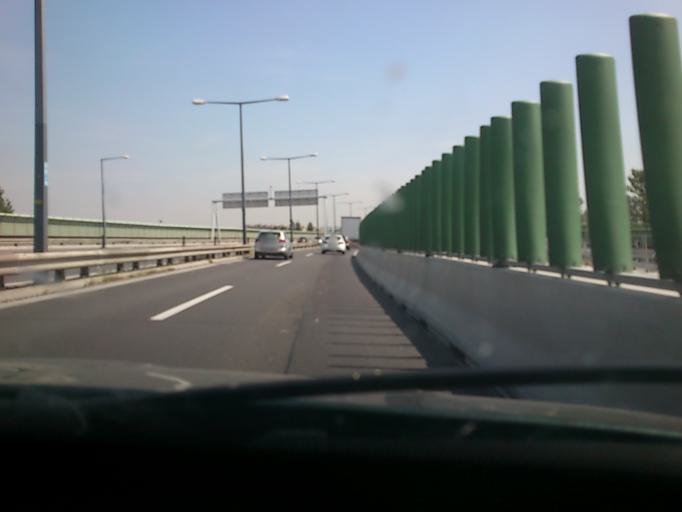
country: AT
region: Lower Austria
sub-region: Politischer Bezirk Modling
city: Vosendorf
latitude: 48.1510
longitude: 16.3457
